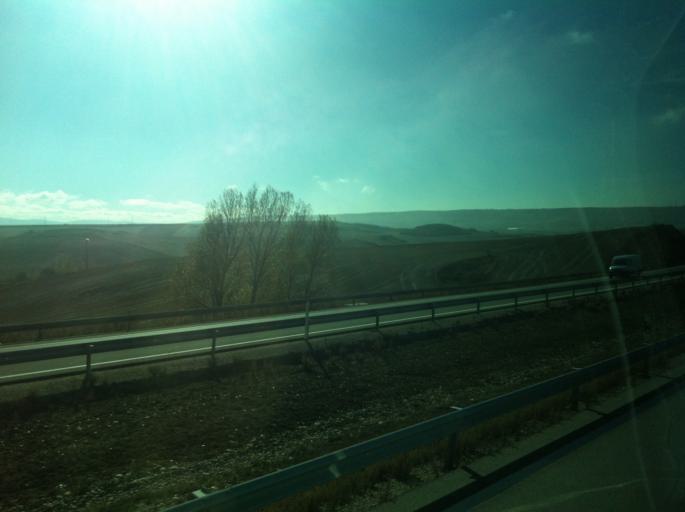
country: ES
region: Castille and Leon
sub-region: Provincia de Burgos
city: Quintanapalla
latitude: 42.4230
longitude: -3.5168
